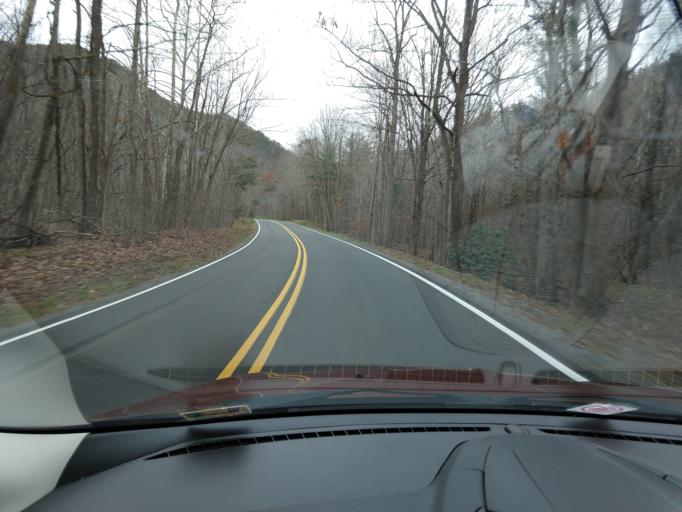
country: US
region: West Virginia
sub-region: Greenbrier County
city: White Sulphur Springs
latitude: 37.7247
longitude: -80.2191
